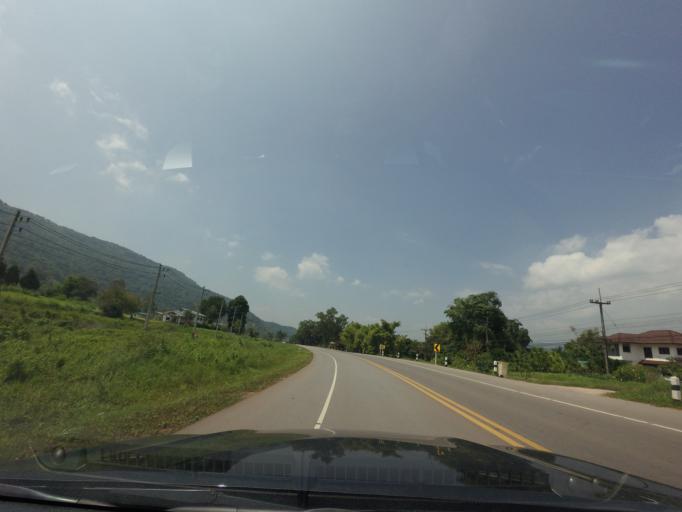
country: TH
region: Loei
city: Phu Ruea
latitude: 17.4592
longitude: 101.4013
